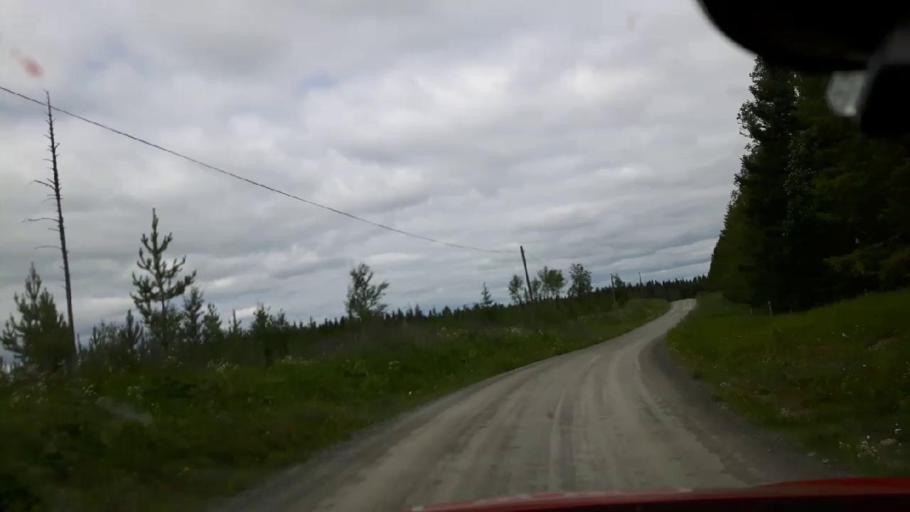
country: SE
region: Jaemtland
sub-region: OEstersunds Kommun
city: Brunflo
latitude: 63.0570
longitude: 14.9120
